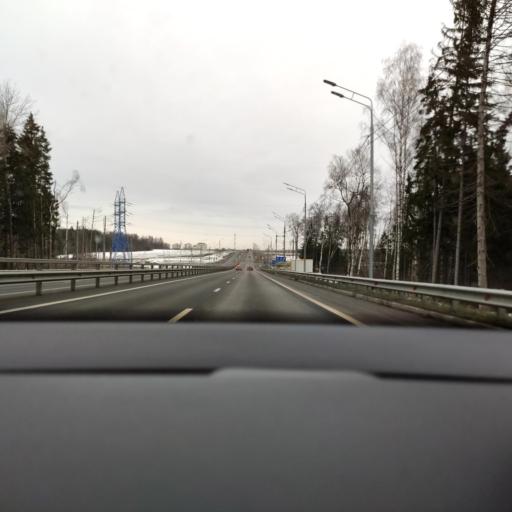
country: RU
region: Moskovskaya
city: Zvenigorod
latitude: 55.6858
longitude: 36.8900
